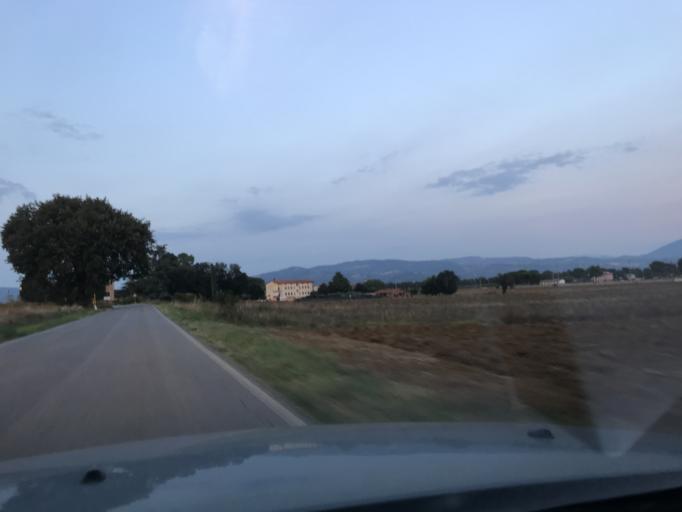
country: IT
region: Umbria
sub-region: Provincia di Perugia
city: Via Lippia
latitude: 43.0939
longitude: 12.4901
